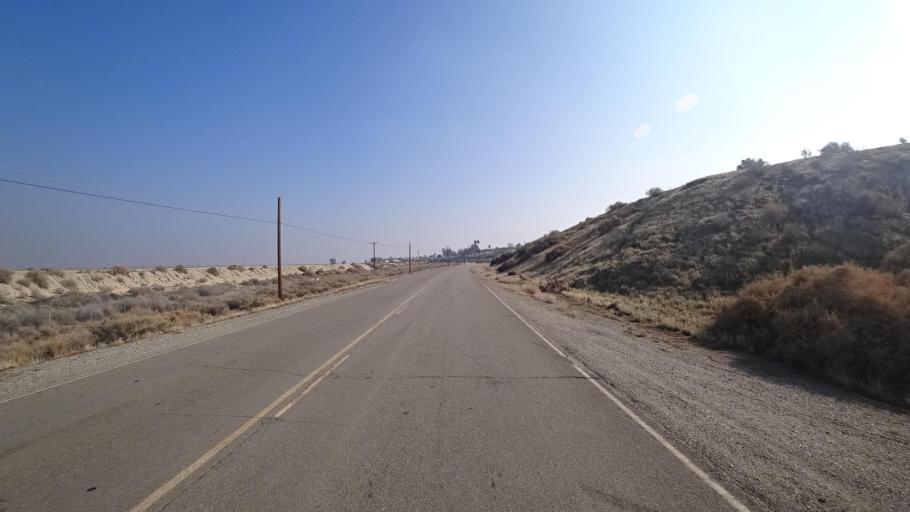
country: US
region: California
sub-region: Kern County
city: Buttonwillow
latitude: 35.3011
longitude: -119.3588
